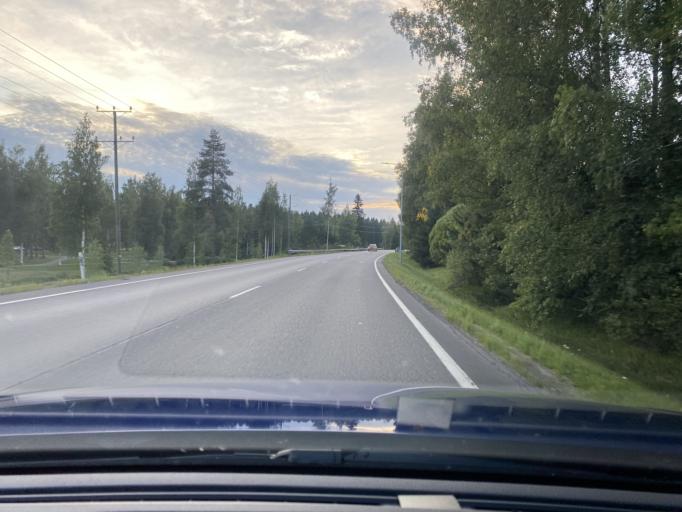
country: FI
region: Satakunta
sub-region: Pohjois-Satakunta
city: Kankaanpaeae
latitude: 61.8051
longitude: 22.3842
